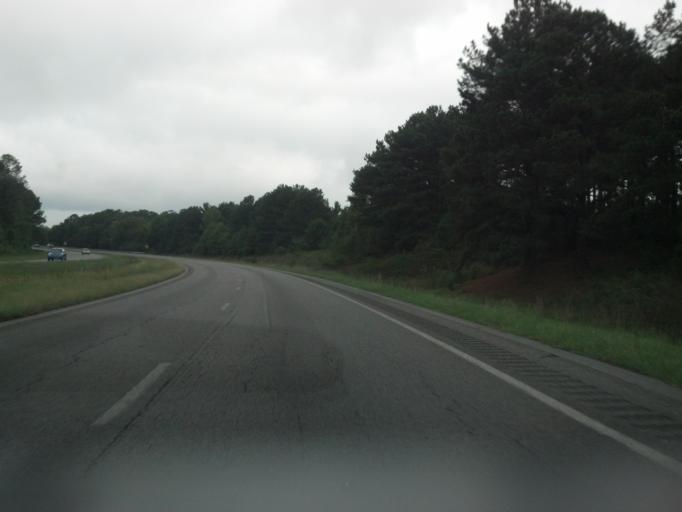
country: US
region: North Carolina
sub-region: Nash County
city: Rocky Mount
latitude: 35.9573
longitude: -77.7665
